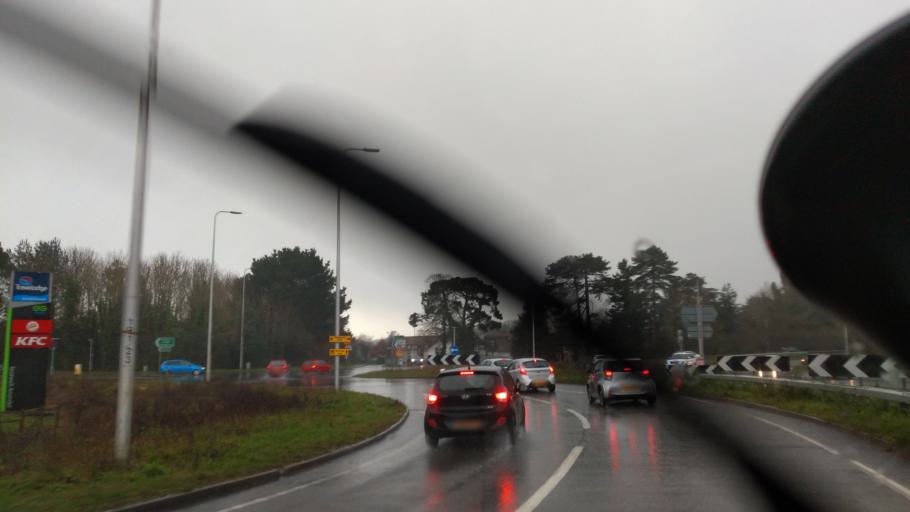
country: GB
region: England
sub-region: West Sussex
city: Fontwell
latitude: 50.8561
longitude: -0.6502
